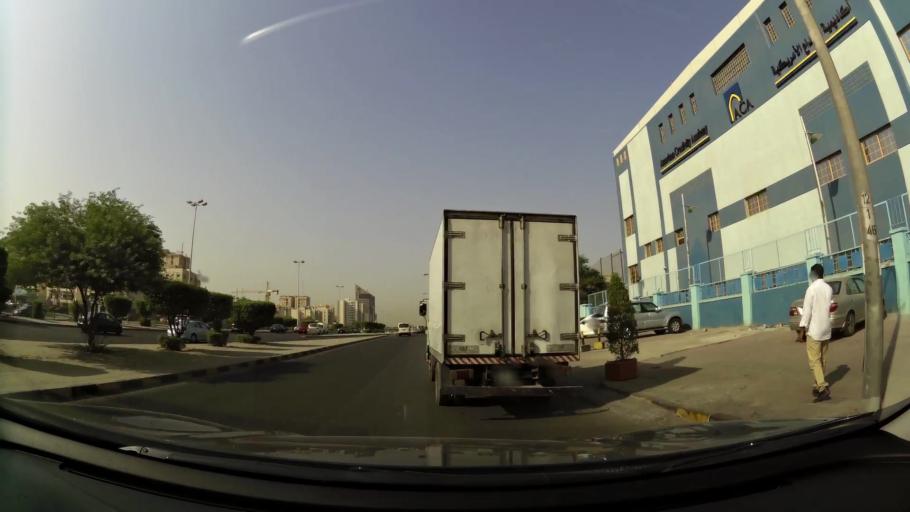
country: KW
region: Muhafazat Hawalli
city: Hawalli
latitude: 29.3266
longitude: 48.0234
